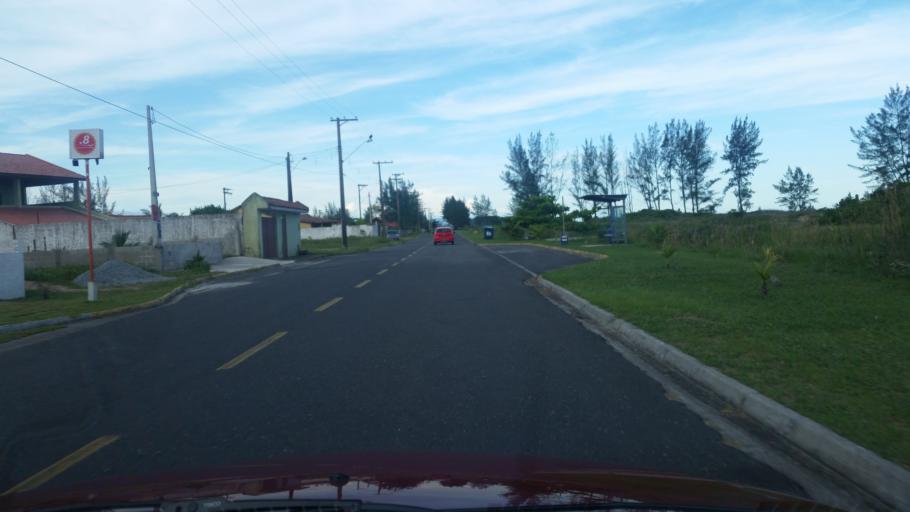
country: BR
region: Sao Paulo
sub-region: Iguape
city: Iguape
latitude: -24.7933
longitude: -47.6191
